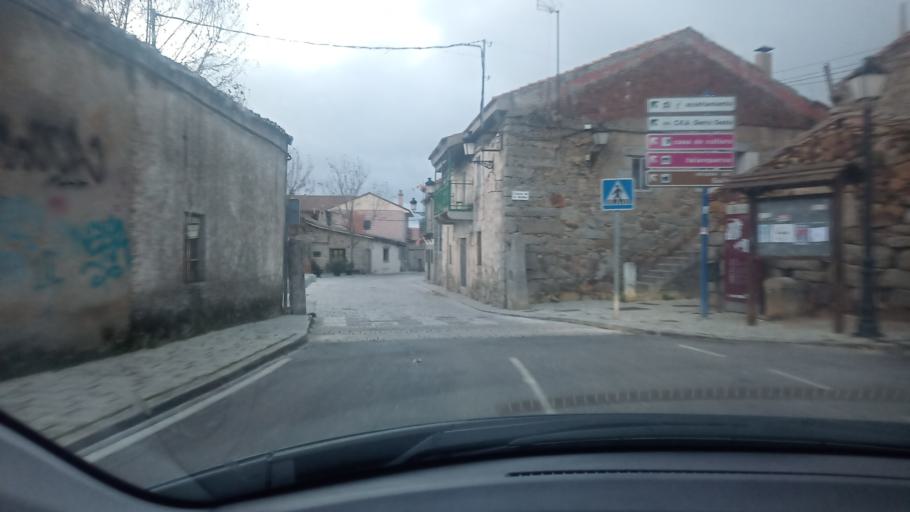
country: ES
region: Madrid
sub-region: Provincia de Madrid
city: Zarzalejo
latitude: 40.5477
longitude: -4.1811
